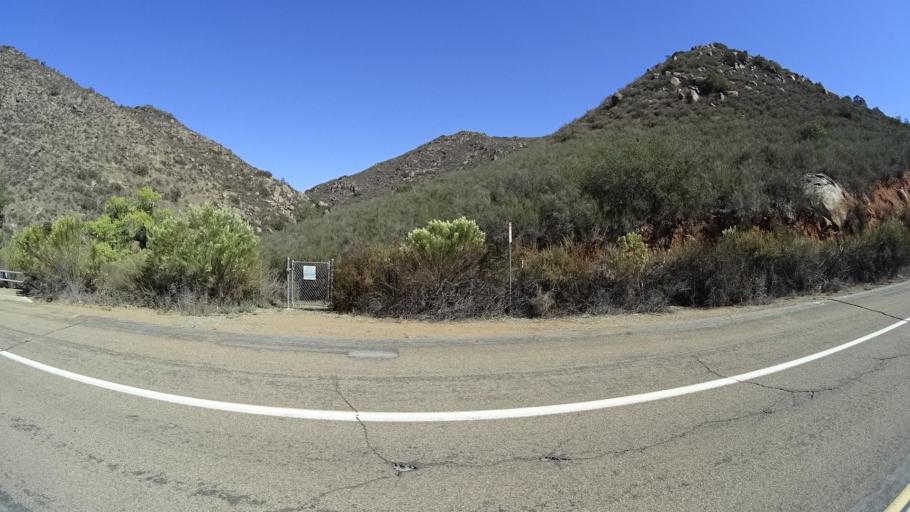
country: US
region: California
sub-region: San Diego County
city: Alpine
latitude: 32.7994
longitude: -116.7486
